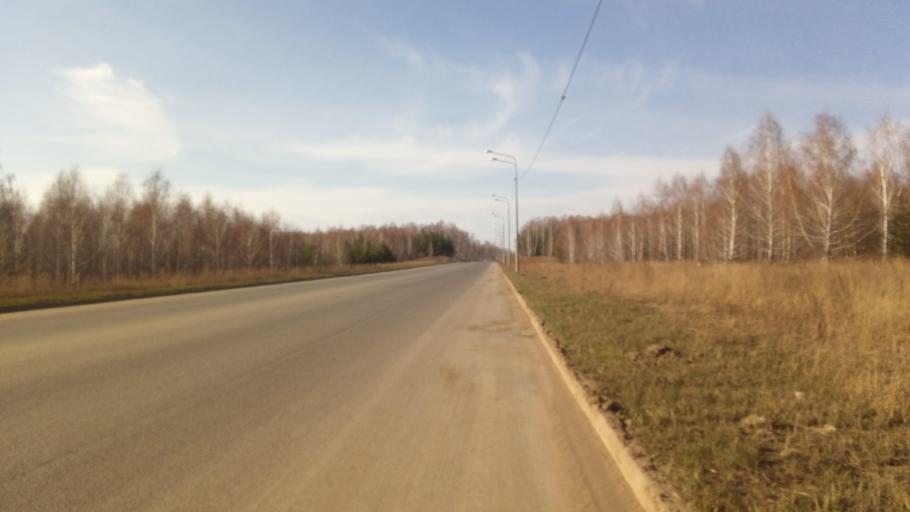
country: RU
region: Chelyabinsk
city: Sargazy
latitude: 55.1166
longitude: 61.2541
